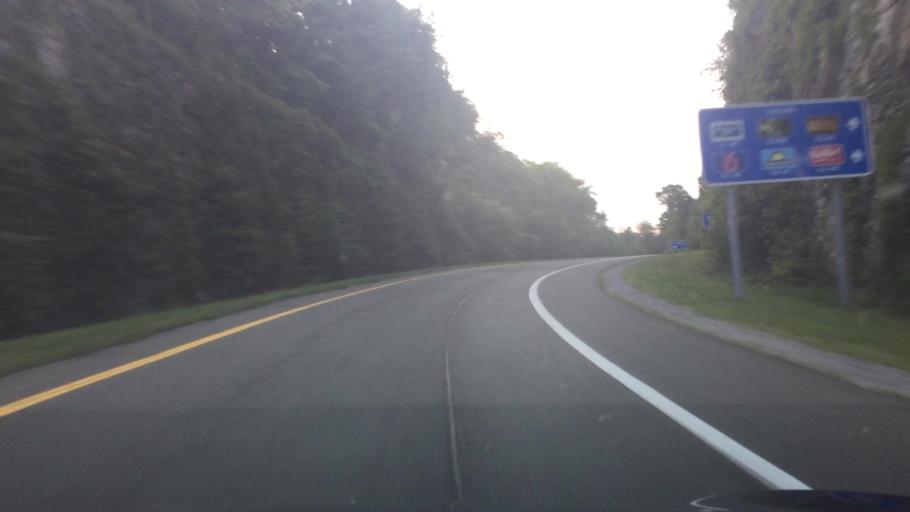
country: US
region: Virginia
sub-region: Wythe County
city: Wytheville
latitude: 36.9470
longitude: -81.0494
